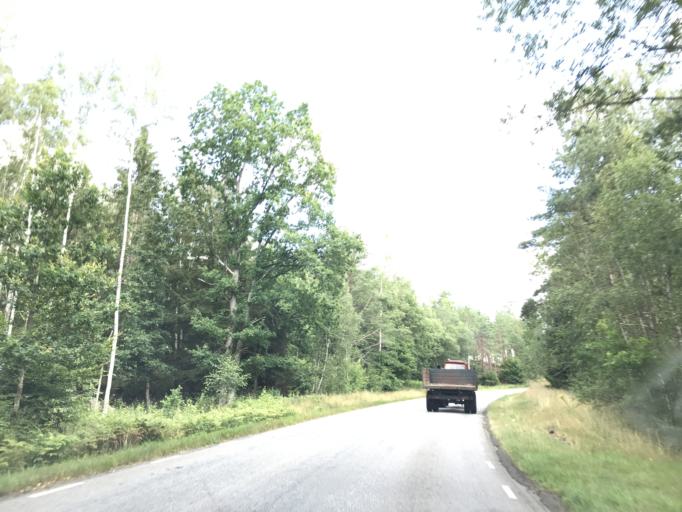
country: SE
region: Halland
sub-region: Laholms Kommun
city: Knared
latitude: 56.4339
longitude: 13.3074
